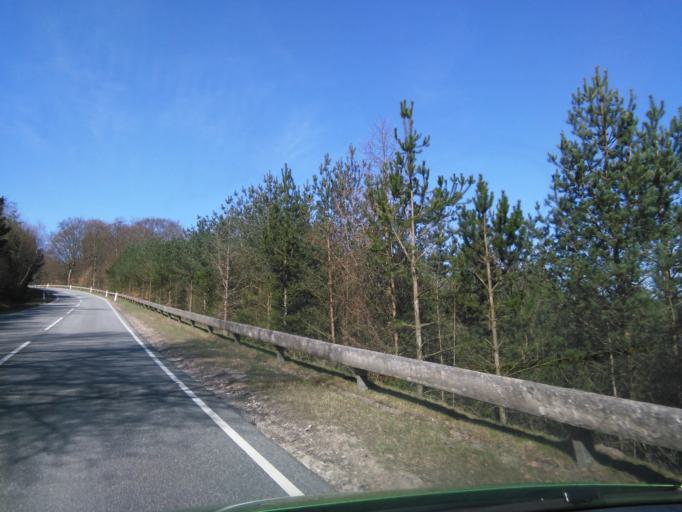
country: DK
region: Central Jutland
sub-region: Horsens Kommune
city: Braedstrup
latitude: 56.0141
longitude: 9.6730
